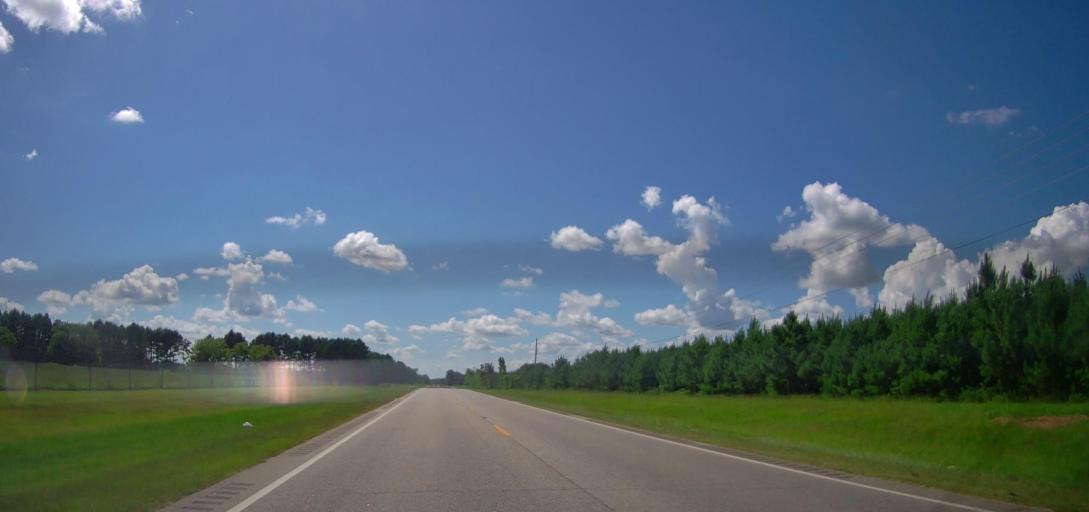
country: US
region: Alabama
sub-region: Elmore County
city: Tallassee
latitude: 32.3882
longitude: -85.8896
